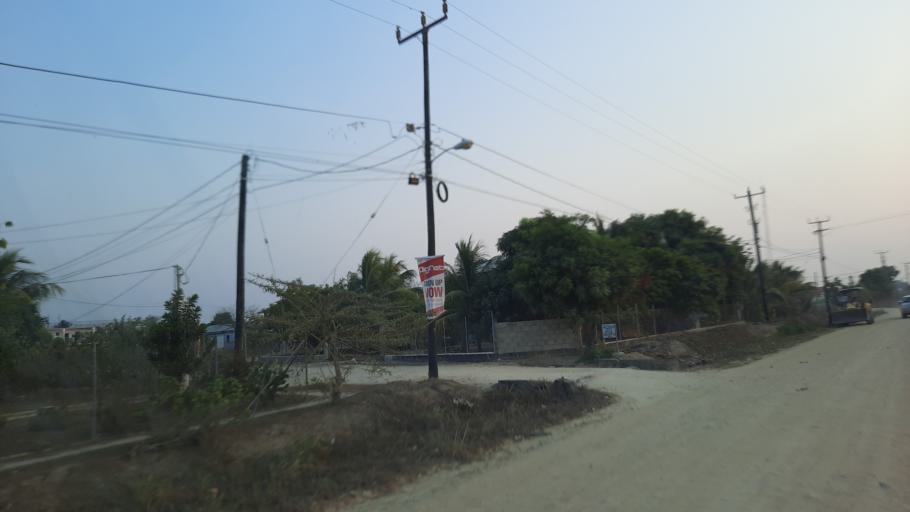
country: BZ
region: Stann Creek
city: Placencia
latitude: 16.5336
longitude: -88.4276
